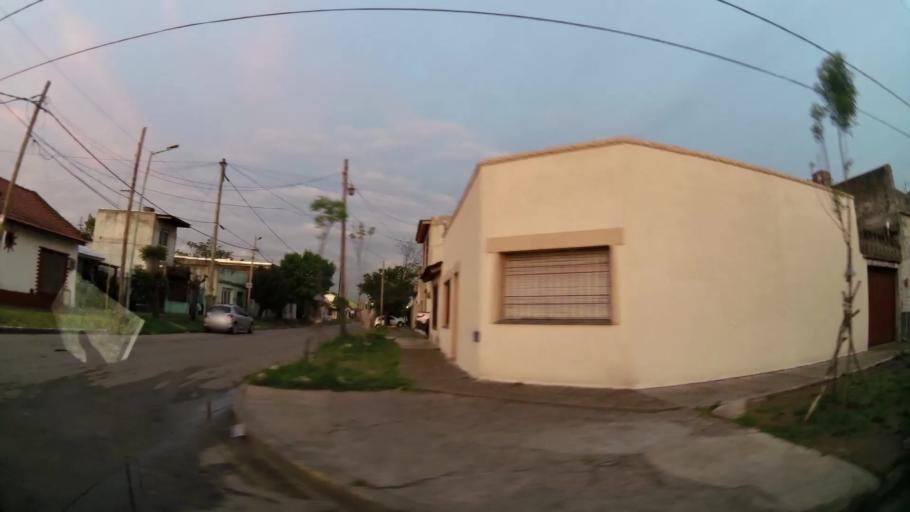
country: AR
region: Buenos Aires
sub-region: Partido de Lomas de Zamora
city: Lomas de Zamora
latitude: -34.7479
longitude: -58.3649
